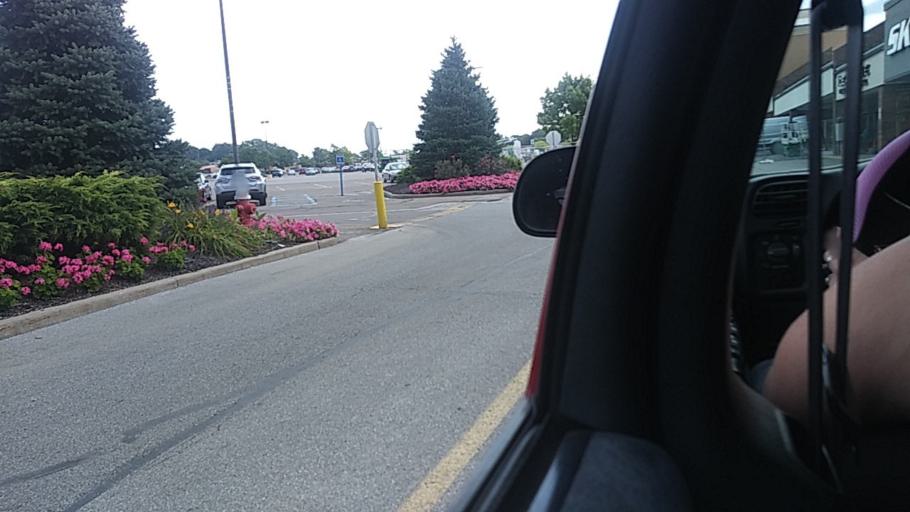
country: US
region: Ohio
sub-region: Summit County
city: Cuyahoga Falls
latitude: 41.1174
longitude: -81.4820
